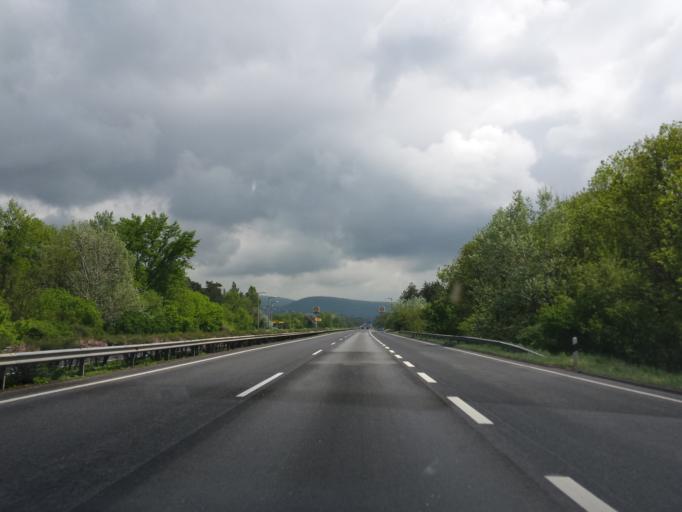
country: HU
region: Komarom-Esztergom
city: Baj
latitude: 47.6189
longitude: 18.3369
